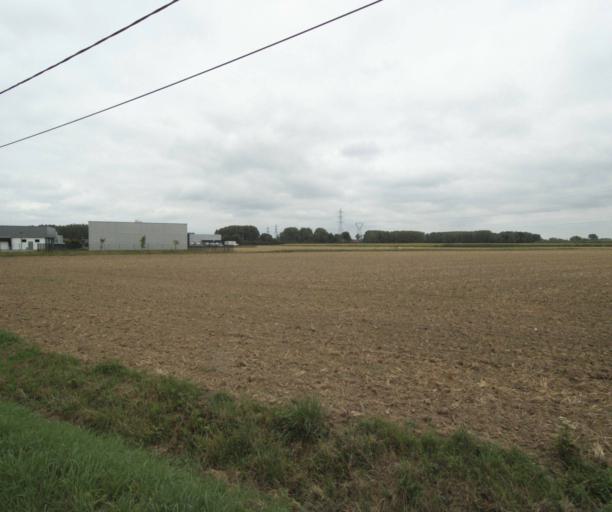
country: FR
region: Nord-Pas-de-Calais
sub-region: Departement du Nord
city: Forest-sur-Marque
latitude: 50.6302
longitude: 3.1941
